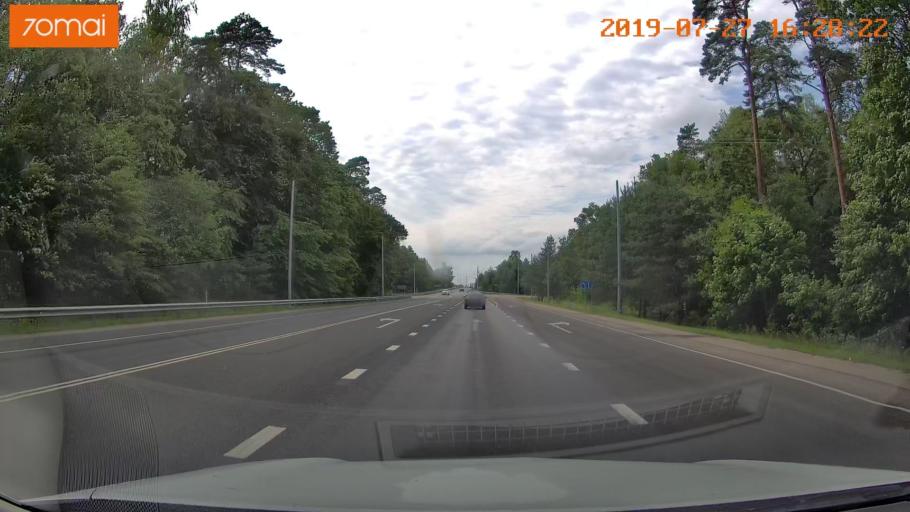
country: RU
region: Kaliningrad
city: Zheleznodorozhnyy
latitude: 54.6477
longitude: 21.3619
